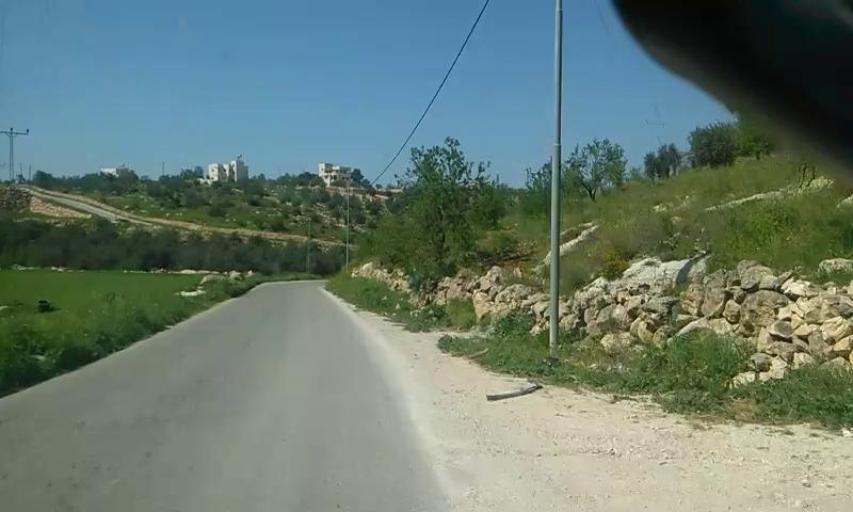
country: PS
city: Bayt Maqdum
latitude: 31.5315
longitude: 34.9768
